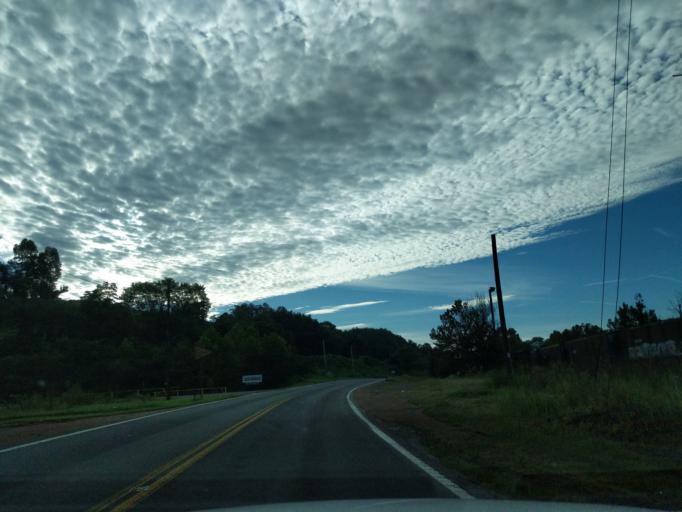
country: US
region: Georgia
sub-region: Fannin County
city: McCaysville
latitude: 34.9927
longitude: -84.3778
